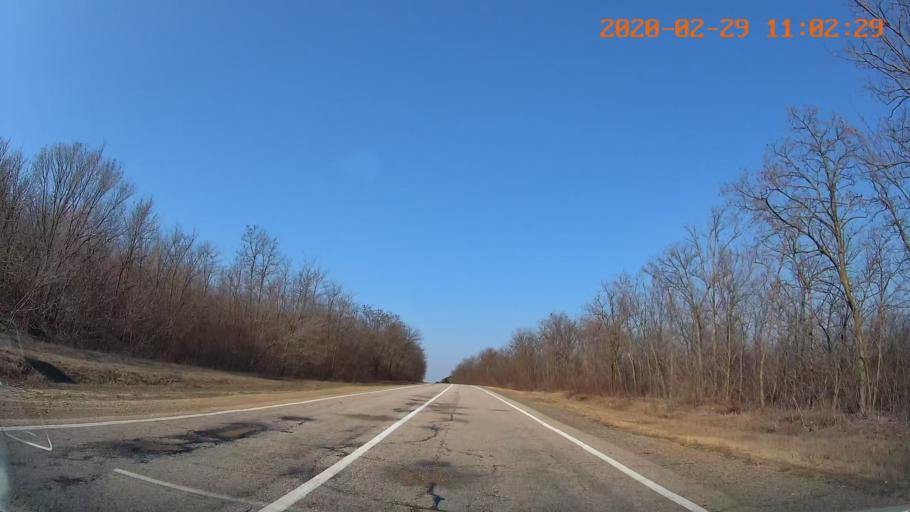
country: MD
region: Telenesti
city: Grigoriopol
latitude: 47.1727
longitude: 29.2373
